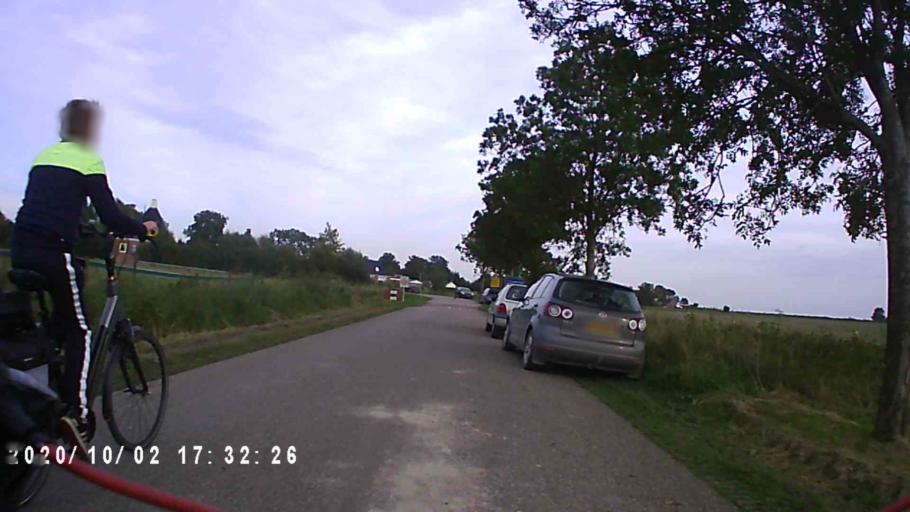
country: NL
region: Groningen
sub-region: Gemeente De Marne
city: Ulrum
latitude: 53.3345
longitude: 6.3358
